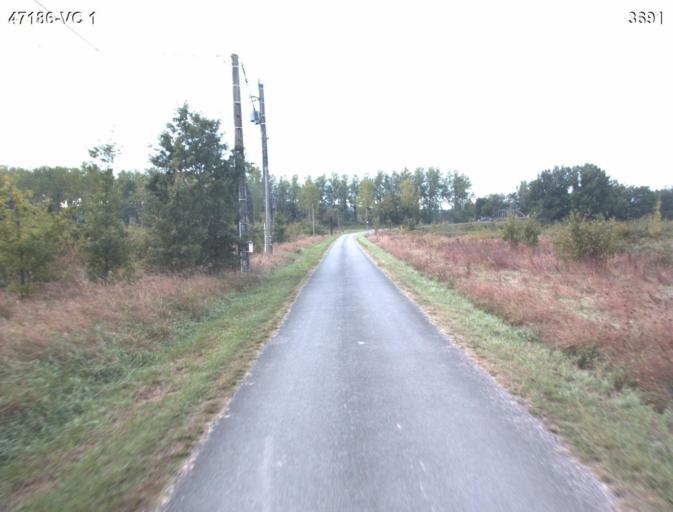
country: FR
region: Aquitaine
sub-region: Departement du Lot-et-Garonne
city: Port-Sainte-Marie
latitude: 44.2191
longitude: 0.4442
